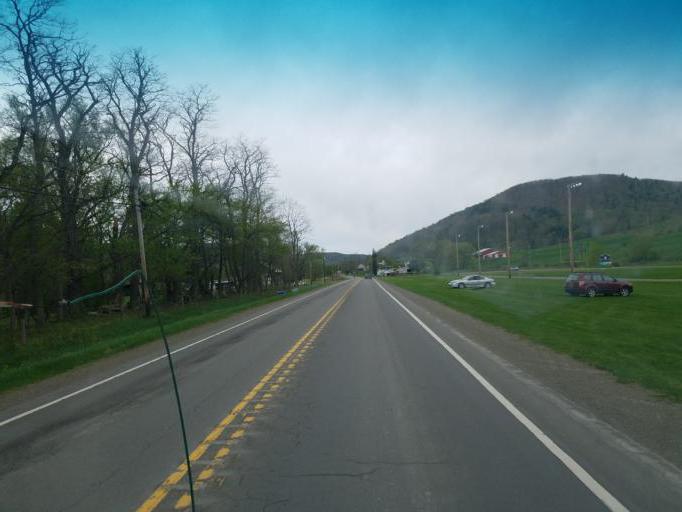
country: US
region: Pennsylvania
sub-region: Tioga County
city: Westfield
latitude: 41.9174
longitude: -77.5669
